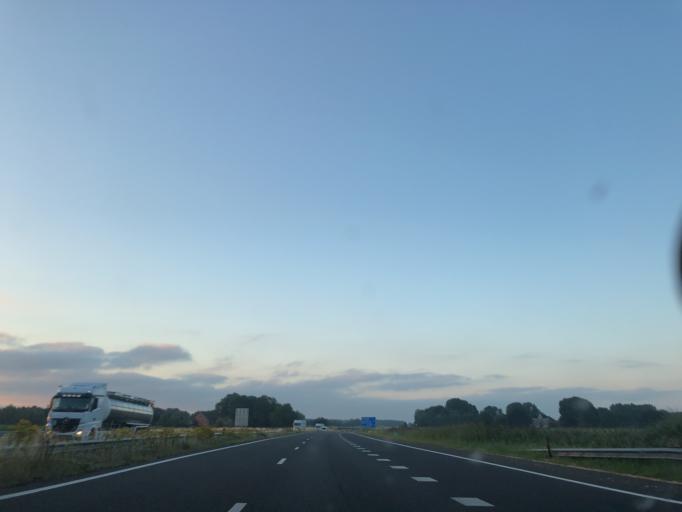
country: NL
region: Groningen
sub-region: Gemeente  Oldambt
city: Winschoten
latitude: 53.1855
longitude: 6.9755
